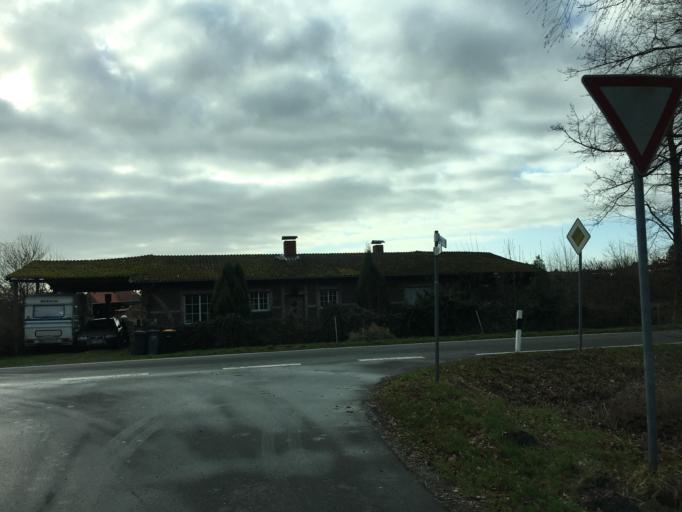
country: DE
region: North Rhine-Westphalia
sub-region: Regierungsbezirk Munster
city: Greven
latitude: 52.0444
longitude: 7.6007
